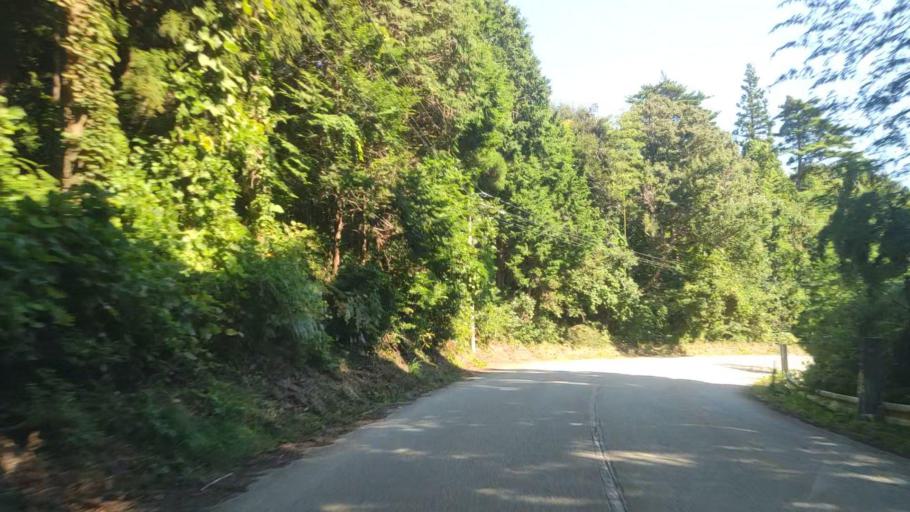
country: JP
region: Ishikawa
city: Nanao
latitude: 37.5097
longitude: 137.3370
